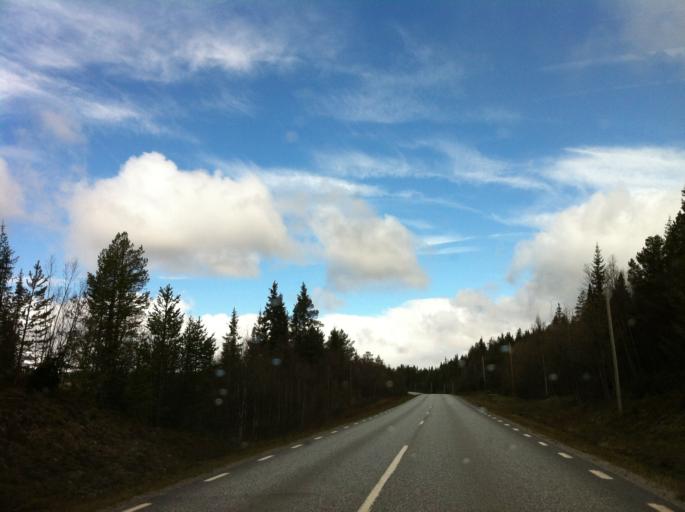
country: SE
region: Jaemtland
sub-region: Are Kommun
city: Are
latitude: 62.5817
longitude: 12.5590
